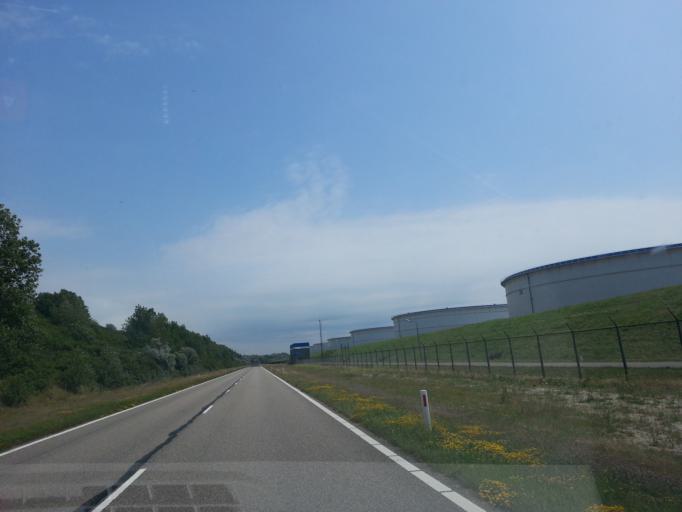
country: NL
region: South Holland
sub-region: Gemeente Rotterdam
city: Hoek van Holland
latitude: 51.9796
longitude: 4.0531
